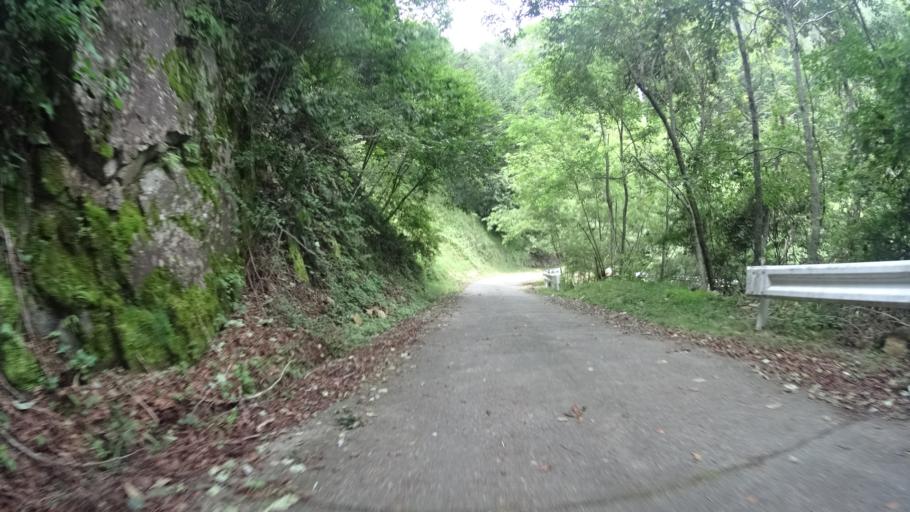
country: JP
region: Yamanashi
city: Kofu-shi
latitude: 35.8284
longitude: 138.5815
